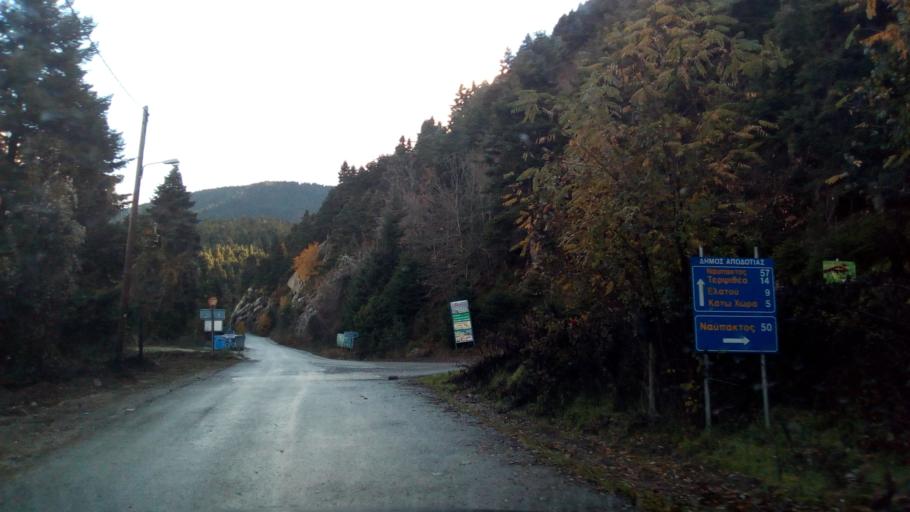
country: GR
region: West Greece
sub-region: Nomos Aitolias kai Akarnanias
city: Nafpaktos
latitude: 38.5875
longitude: 21.9294
